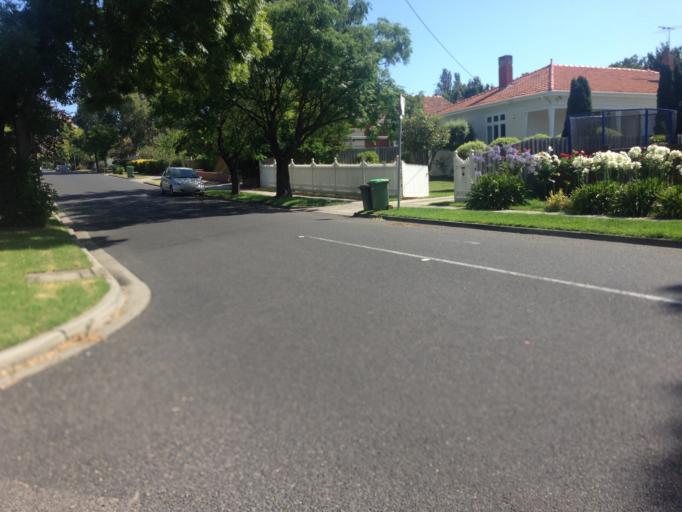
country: AU
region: Victoria
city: Ivanhoe East
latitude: -37.7724
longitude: 145.0467
